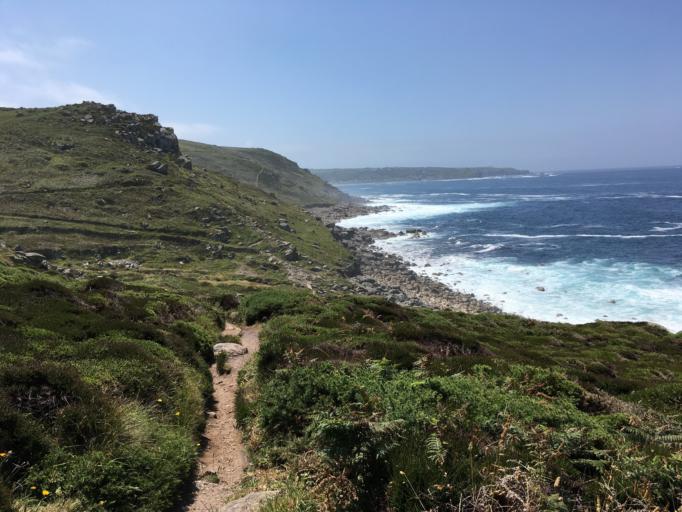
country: GB
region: England
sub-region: Cornwall
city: Saint Just
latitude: 50.1064
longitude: -5.6968
